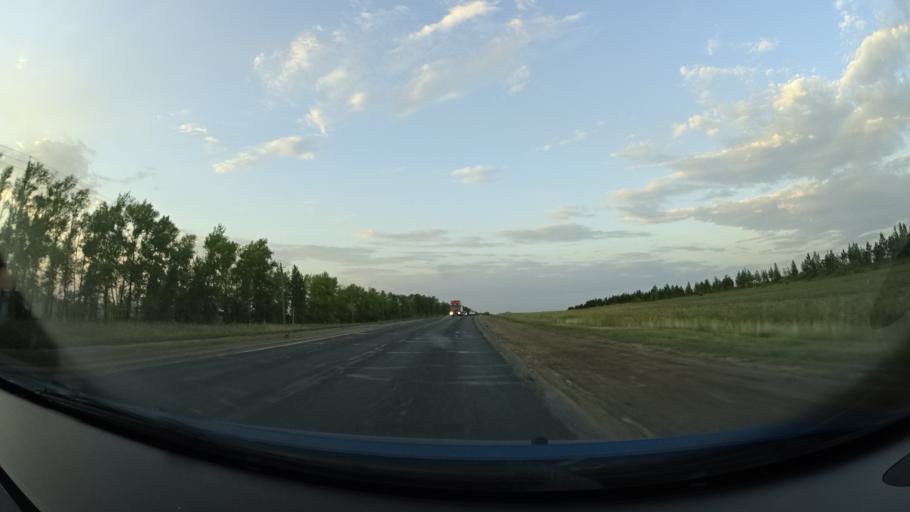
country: RU
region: Orenburg
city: Severnoye
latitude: 54.2077
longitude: 52.6999
